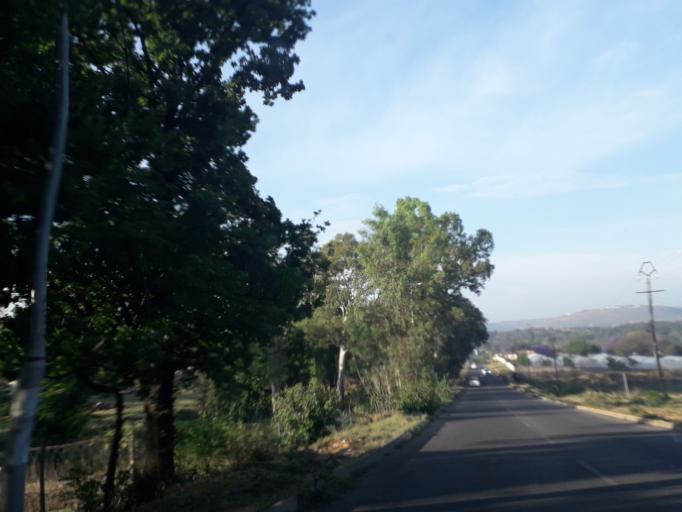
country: ZA
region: Gauteng
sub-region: West Rand District Municipality
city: Muldersdriseloop
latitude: -26.0777
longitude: 27.9092
